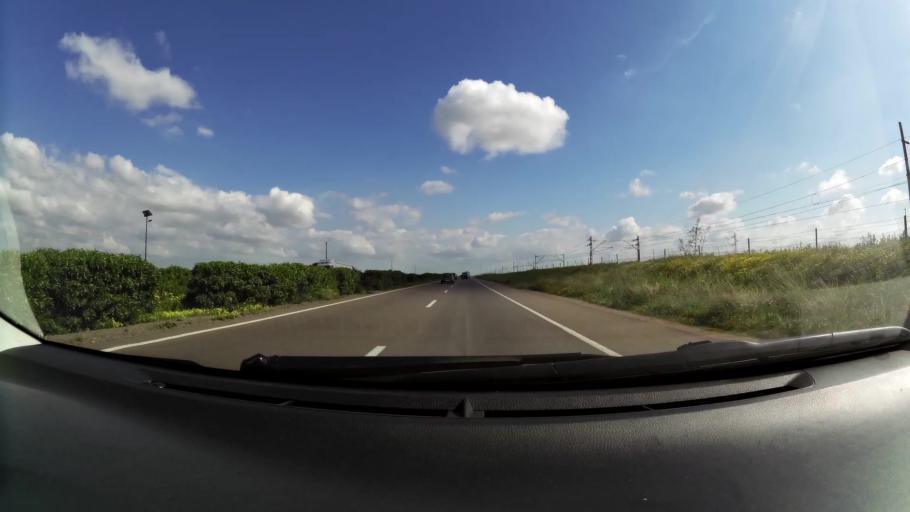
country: MA
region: Chaouia-Ouardigha
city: Nouaseur
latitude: 33.3548
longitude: -7.6175
